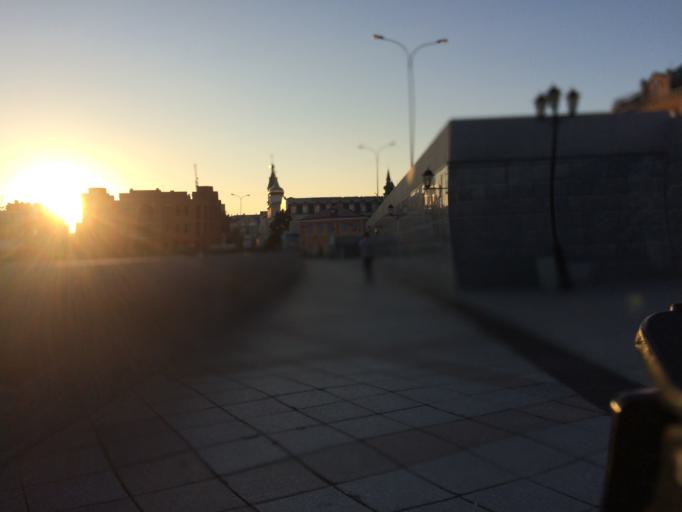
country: RU
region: Mariy-El
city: Yoshkar-Ola
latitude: 56.6324
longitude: 47.9023
